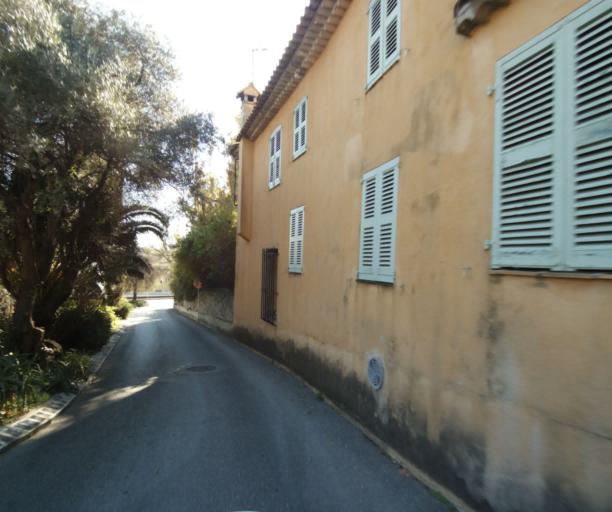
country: FR
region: Provence-Alpes-Cote d'Azur
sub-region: Departement des Alpes-Maritimes
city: Antibes
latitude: 43.5880
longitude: 7.1155
